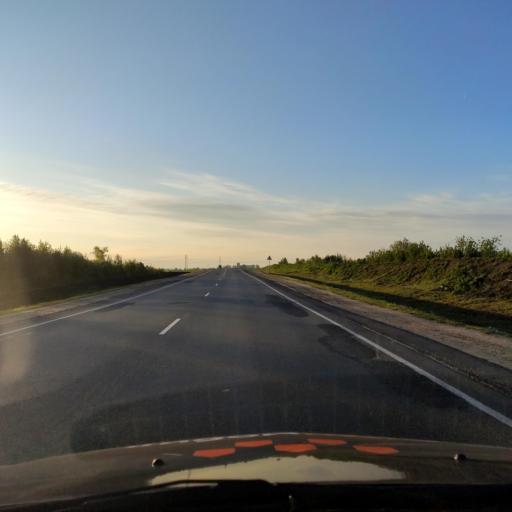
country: RU
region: Orjol
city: Livny
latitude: 52.4412
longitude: 37.5485
